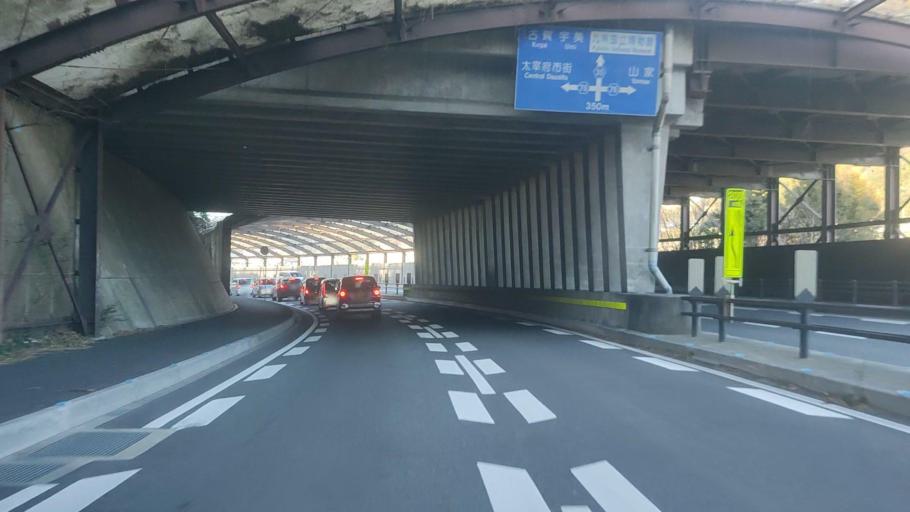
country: JP
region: Fukuoka
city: Dazaifu
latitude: 33.5131
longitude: 130.5483
